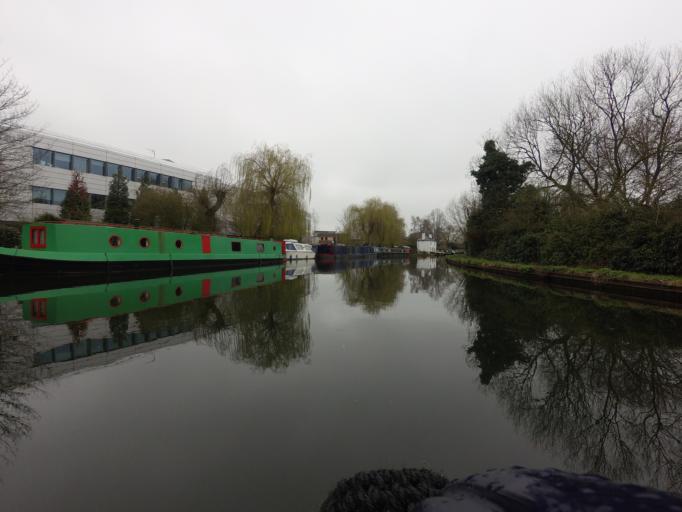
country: GB
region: England
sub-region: Hertfordshire
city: Kings Langley
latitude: 51.7080
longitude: -0.4416
